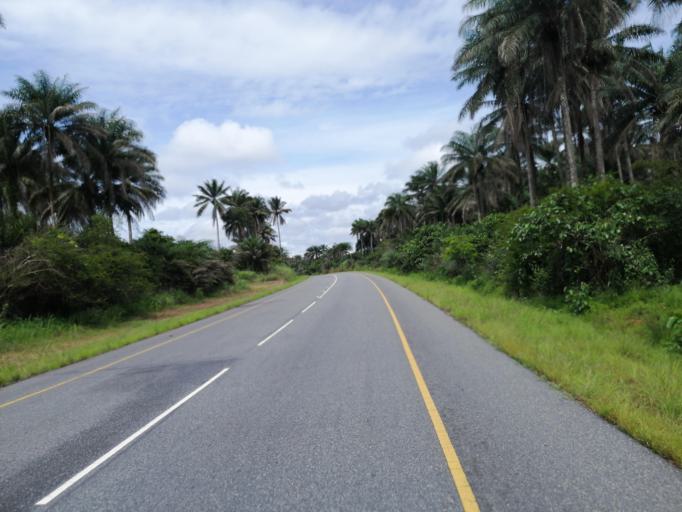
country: SL
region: Northern Province
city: Pepel
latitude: 8.7197
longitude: -12.9601
